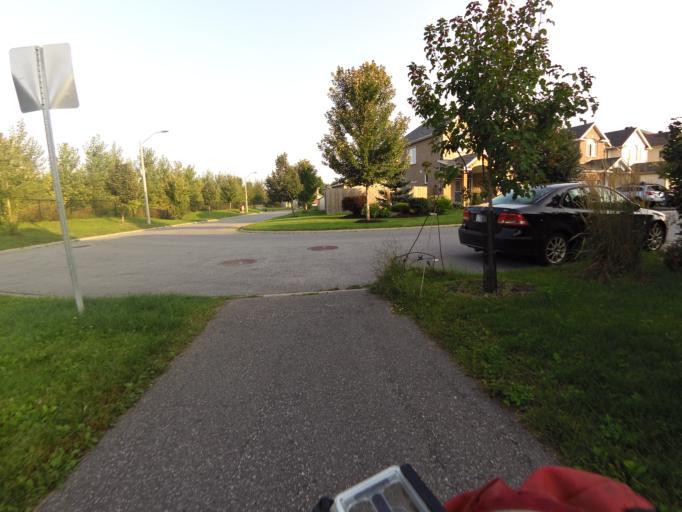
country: CA
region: Ontario
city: Bells Corners
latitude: 45.3582
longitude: -75.9213
